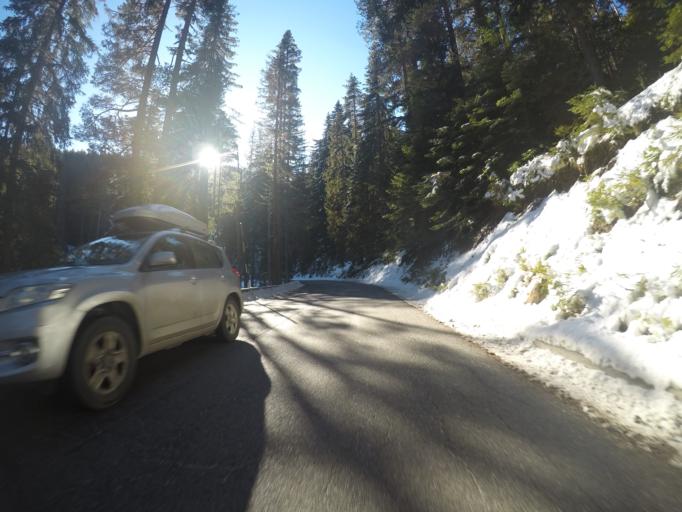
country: BG
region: Blagoevgrad
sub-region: Obshtina Bansko
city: Bansko
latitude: 41.7842
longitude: 23.4530
